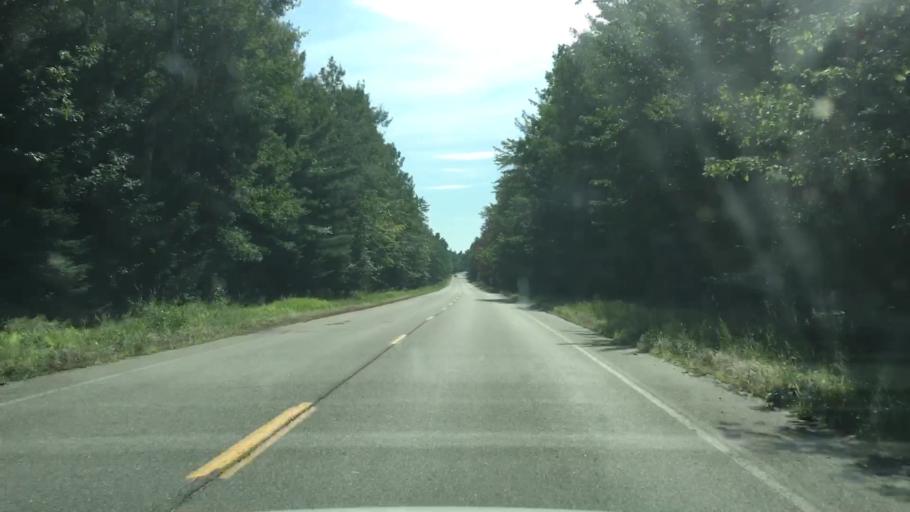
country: US
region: Maine
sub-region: Penobscot County
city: Lincoln
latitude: 45.3879
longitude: -68.5367
